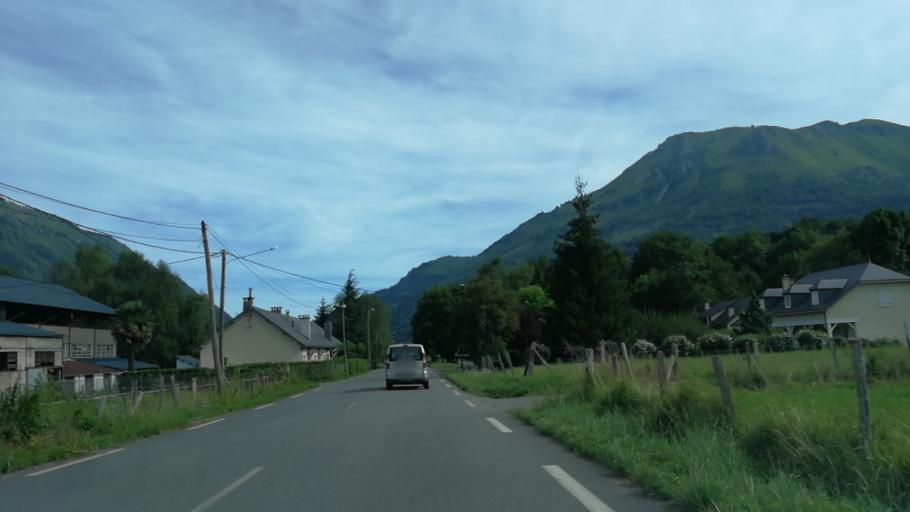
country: FR
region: Aquitaine
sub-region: Departement des Pyrenees-Atlantiques
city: Arette
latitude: 42.9835
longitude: -0.6049
